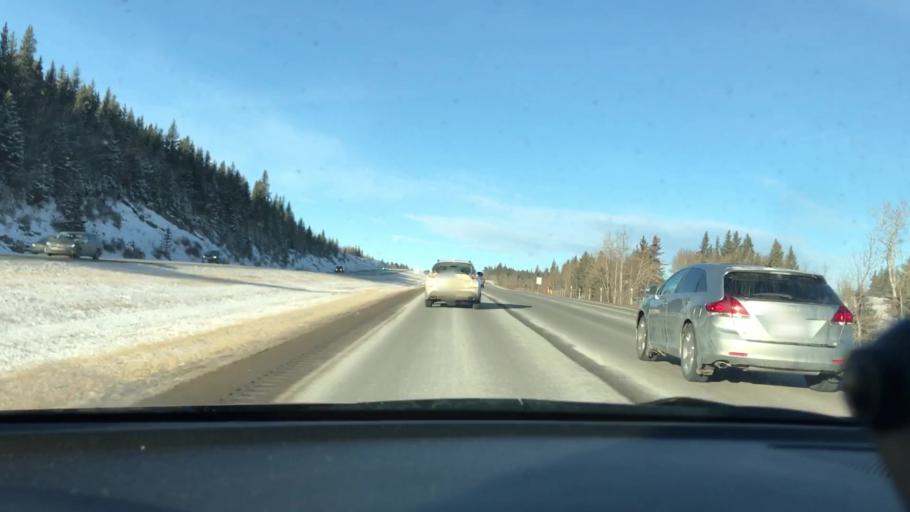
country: CA
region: Alberta
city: Cochrane
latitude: 51.1362
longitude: -114.7067
